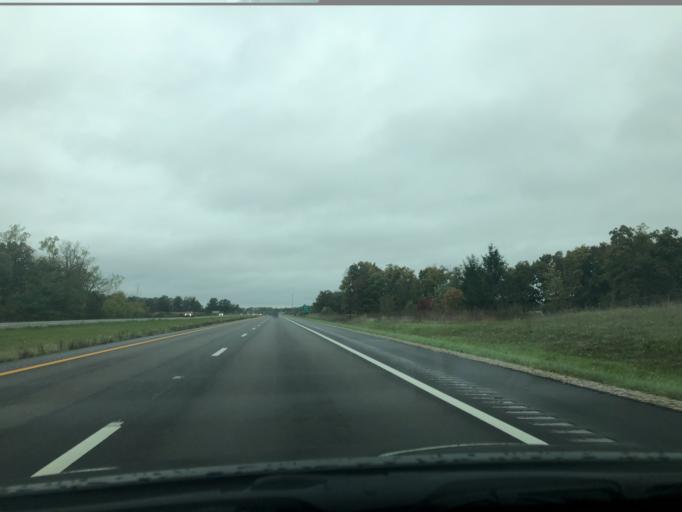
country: US
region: Ohio
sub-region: Champaign County
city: North Lewisburg
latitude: 40.2613
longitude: -83.4761
